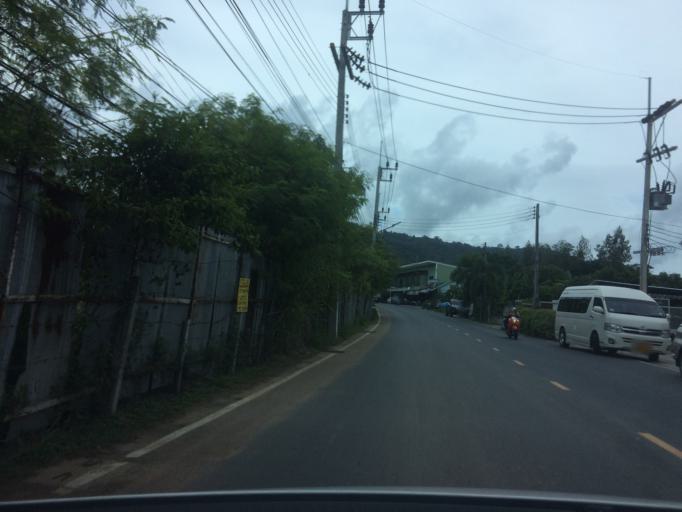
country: TH
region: Phuket
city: Mueang Phuket
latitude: 7.8656
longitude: 98.3575
